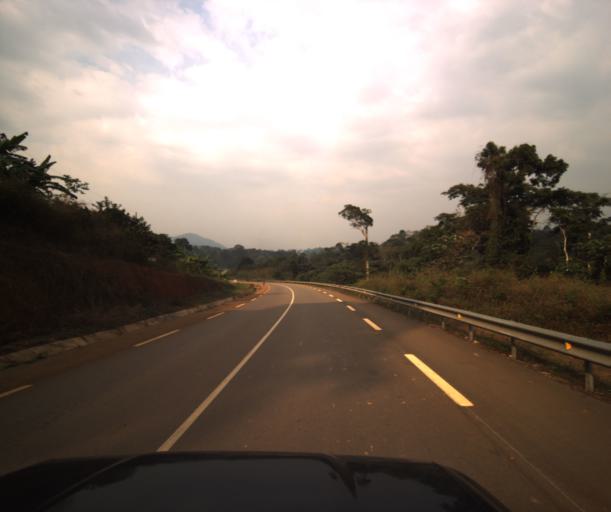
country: CM
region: Centre
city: Mbankomo
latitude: 3.7700
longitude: 11.4138
